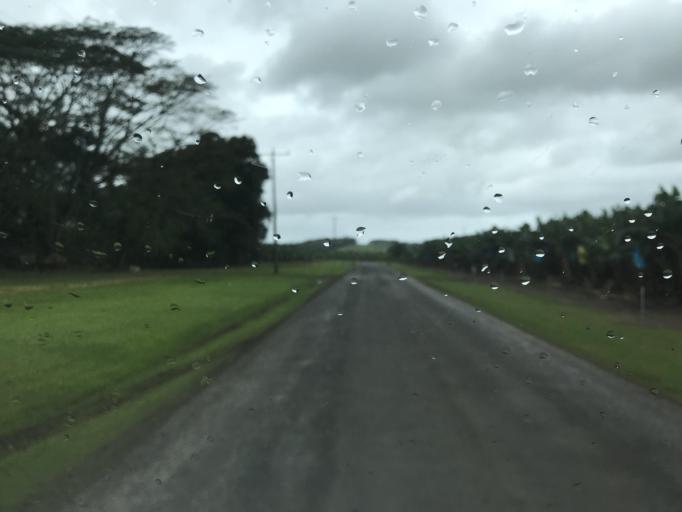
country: AU
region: Queensland
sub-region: Cassowary Coast
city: Innisfail
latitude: -17.5031
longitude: 145.9812
